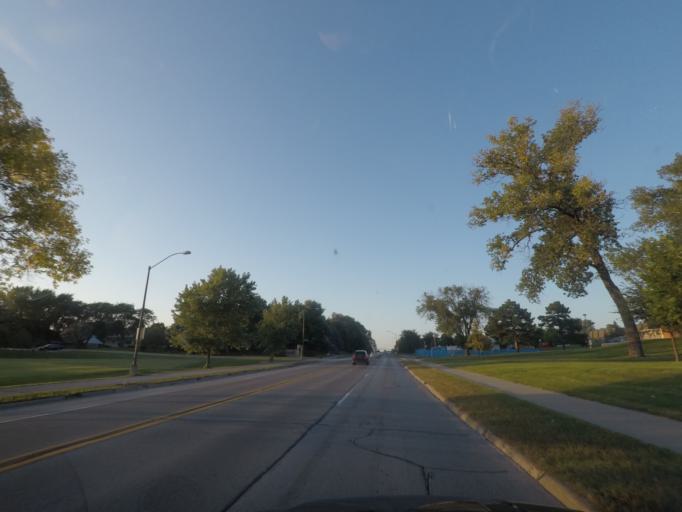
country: US
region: Iowa
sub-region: Story County
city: Ames
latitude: 42.0409
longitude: -93.6448
